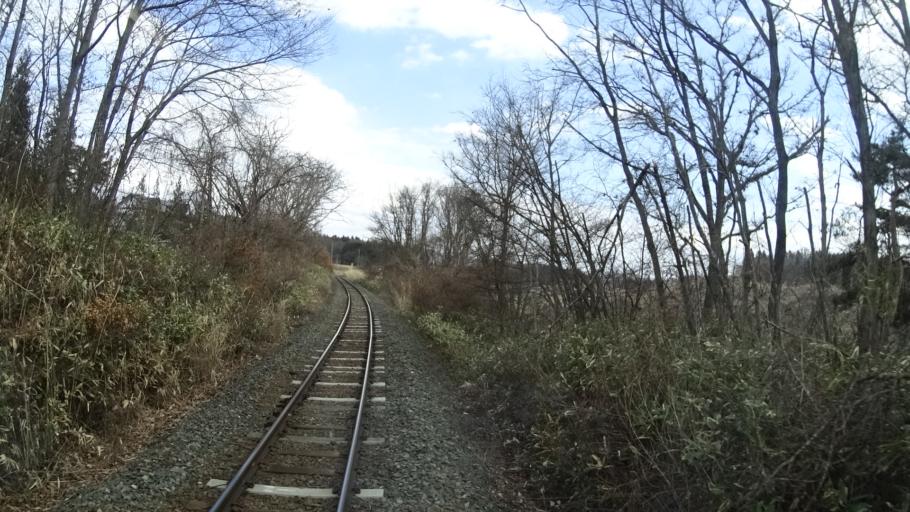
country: JP
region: Iwate
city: Hanamaki
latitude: 39.4070
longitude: 141.1975
